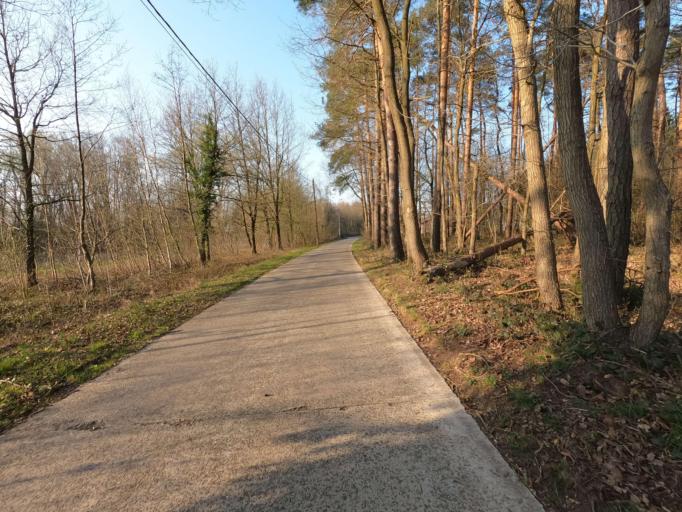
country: BE
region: Flanders
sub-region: Provincie Vlaams-Brabant
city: Aarschot
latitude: 51.0128
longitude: 4.8468
